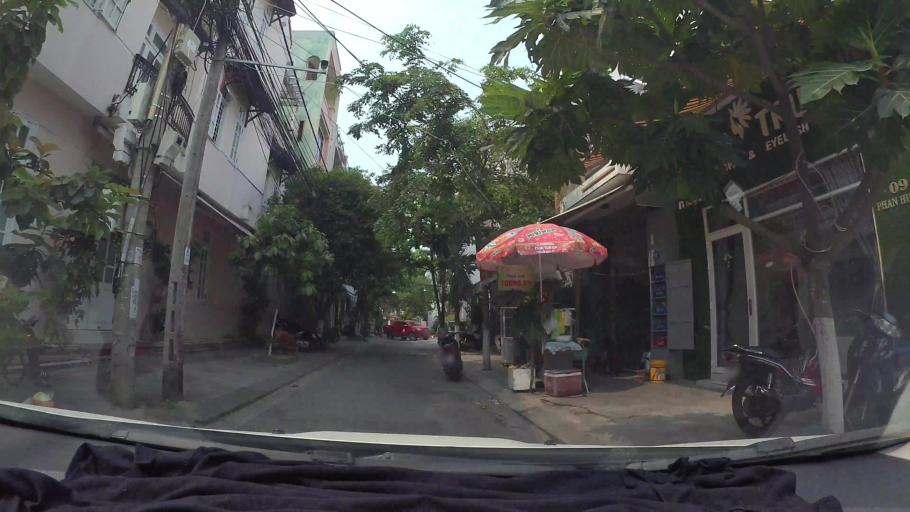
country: VN
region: Da Nang
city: Cam Le
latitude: 16.0386
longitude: 108.2189
